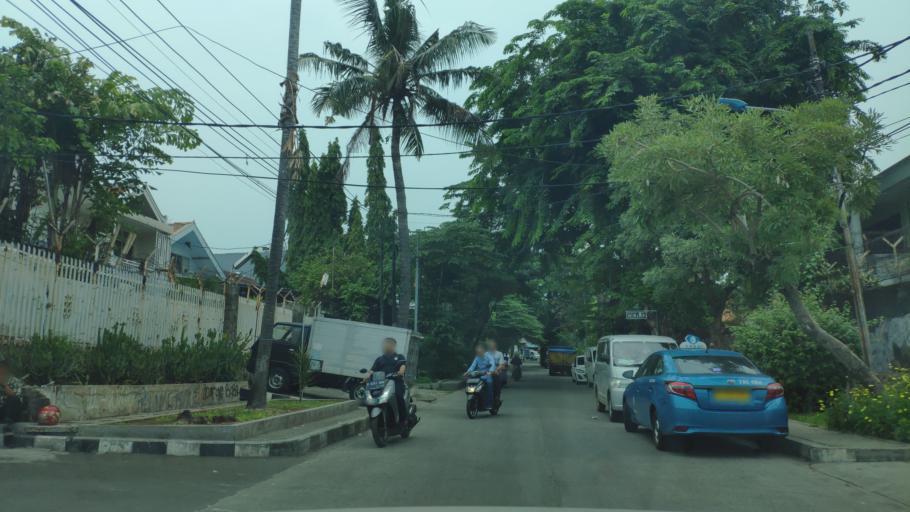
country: ID
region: Jakarta Raya
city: Jakarta
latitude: -6.1914
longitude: 106.8032
